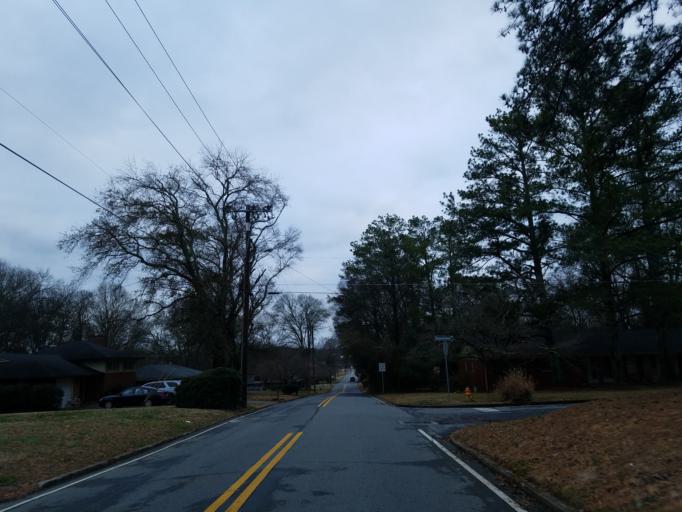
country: US
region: Georgia
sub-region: Bartow County
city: Cartersville
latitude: 34.1568
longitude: -84.7989
